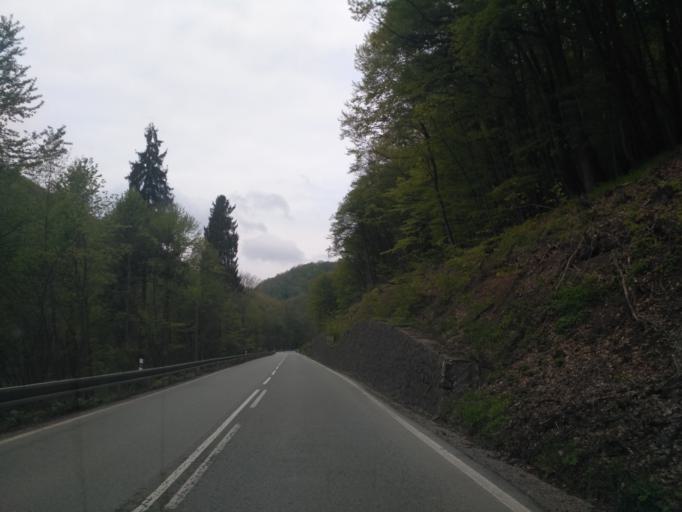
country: SK
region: Kosicky
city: Kosice
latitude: 48.7521
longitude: 21.2199
